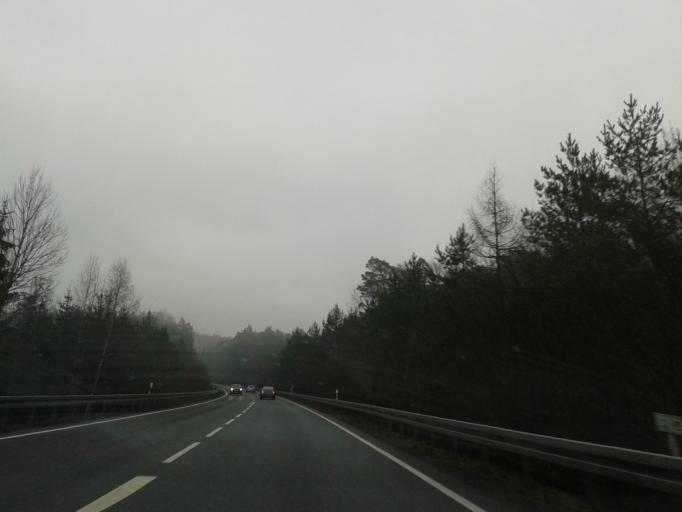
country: DE
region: Bavaria
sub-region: Regierungsbezirk Unterfranken
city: Burgpreppach
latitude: 50.1569
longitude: 10.6842
